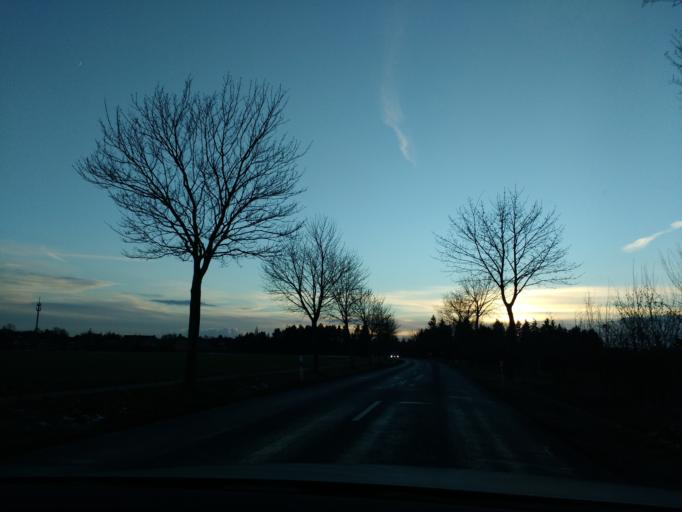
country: DE
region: Lower Saxony
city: Schwarmstedt
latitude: 52.6858
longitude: 9.6240
